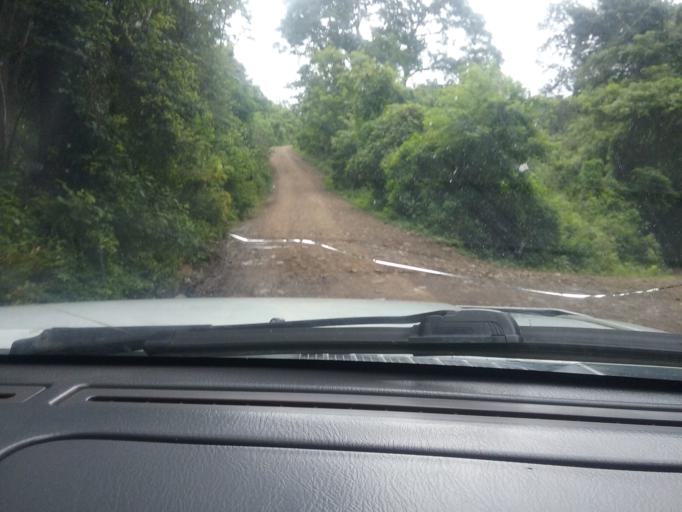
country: NI
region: Matagalpa
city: Matagalpa
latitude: 12.8733
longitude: -85.9565
